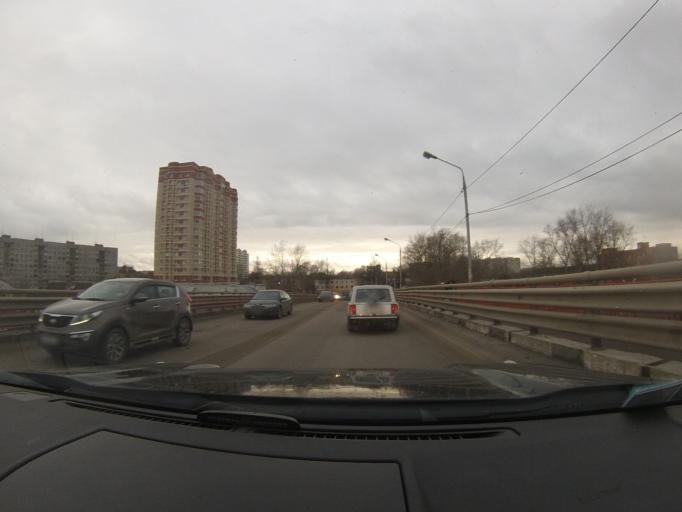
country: RU
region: Moskovskaya
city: Voskresensk
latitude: 55.3260
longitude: 38.6848
